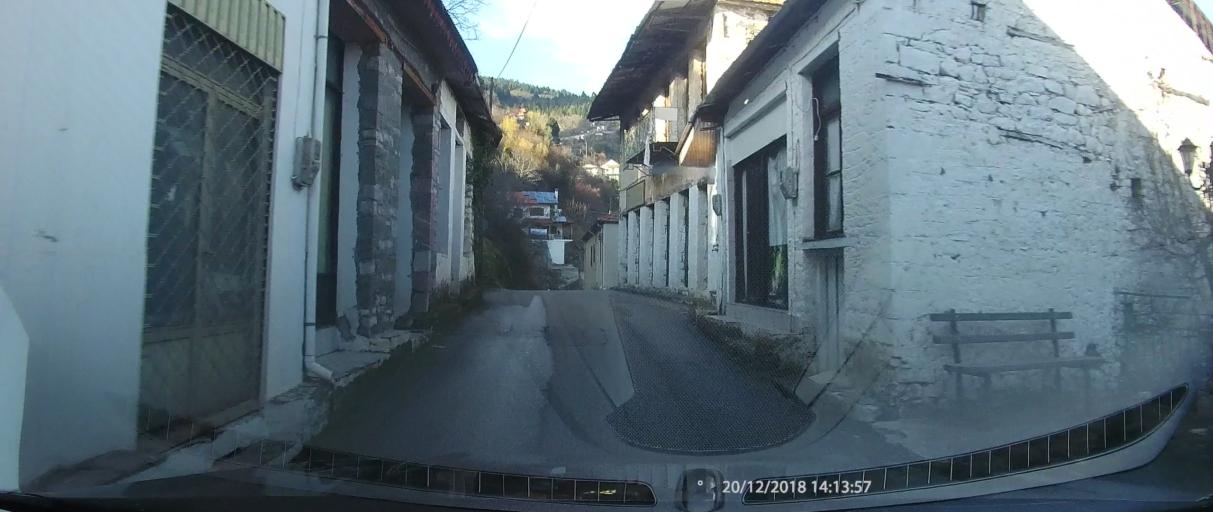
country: GR
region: West Greece
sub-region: Nomos Aitolias kai Akarnanias
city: Thermo
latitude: 38.7444
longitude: 21.6535
